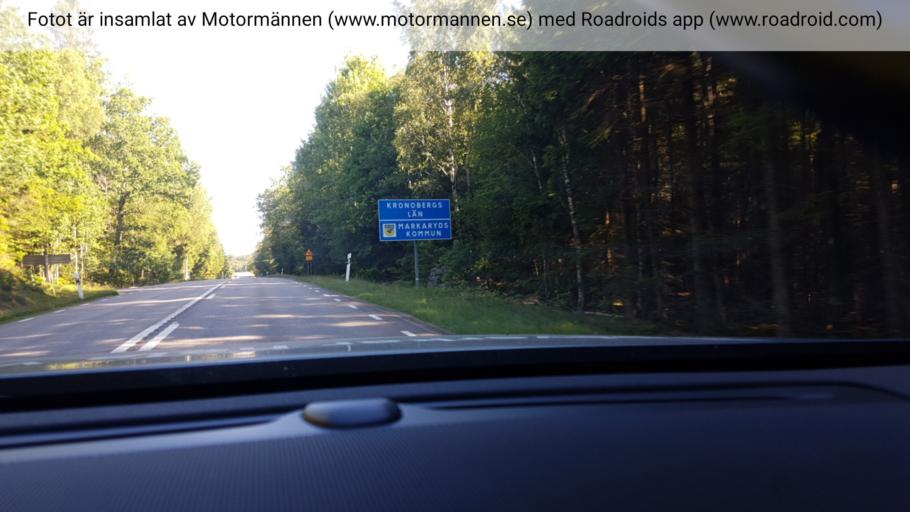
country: SE
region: Kronoberg
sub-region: Markaryds Kommun
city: Markaryd
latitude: 56.4178
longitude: 13.6280
